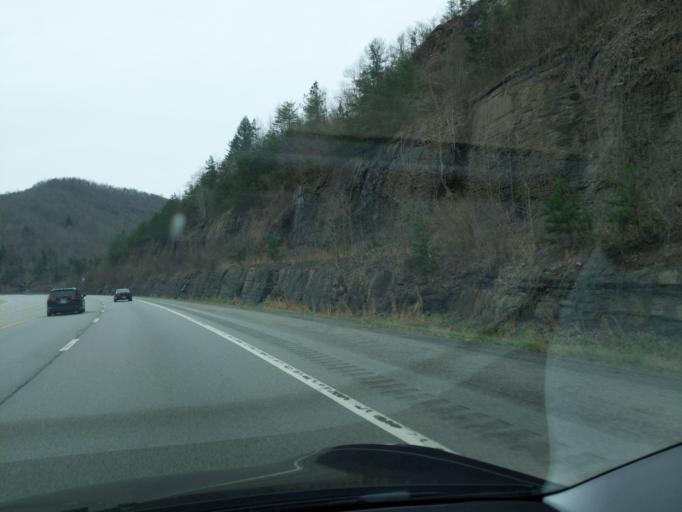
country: US
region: Kentucky
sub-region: Bell County
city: Pineville
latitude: 36.7770
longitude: -83.7370
